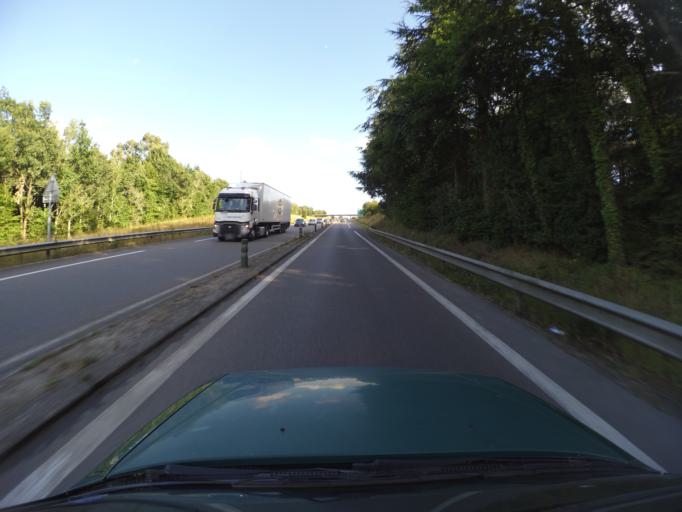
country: FR
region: Pays de la Loire
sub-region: Departement de la Loire-Atlantique
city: Les Sorinieres
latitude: 47.1781
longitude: -1.5165
